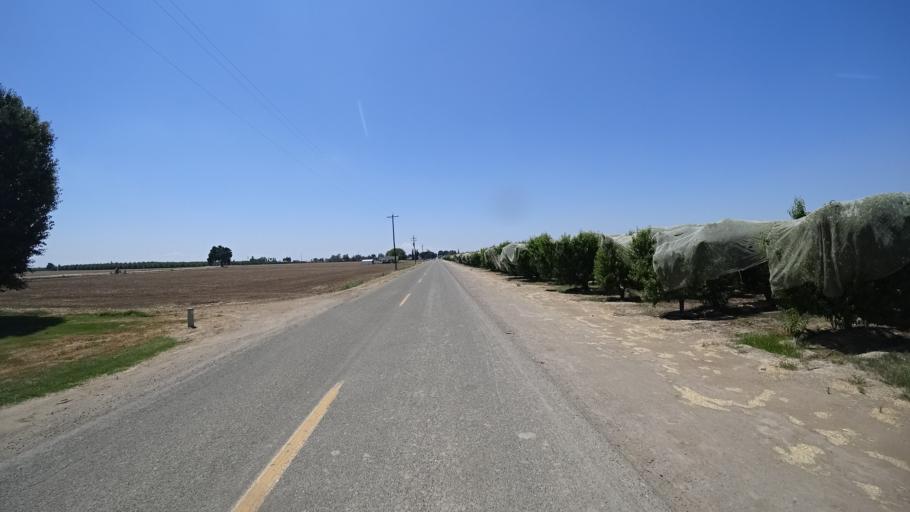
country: US
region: California
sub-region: Kings County
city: Lucerne
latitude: 36.3865
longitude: -119.6421
